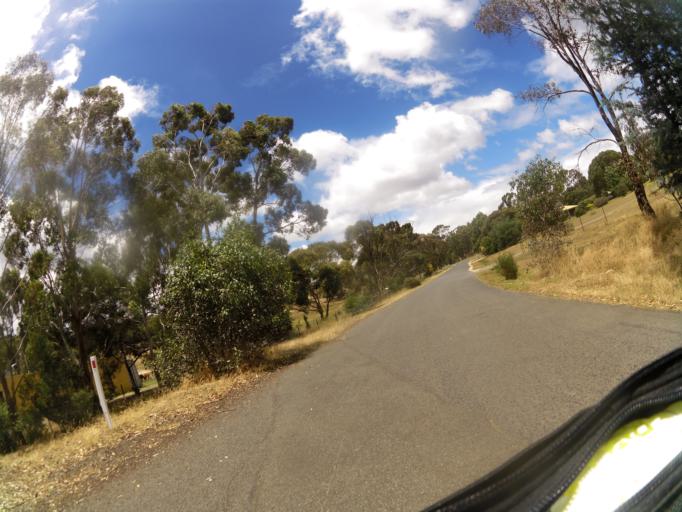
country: AU
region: Victoria
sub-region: Mount Alexander
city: Castlemaine
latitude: -37.0206
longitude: 144.2465
